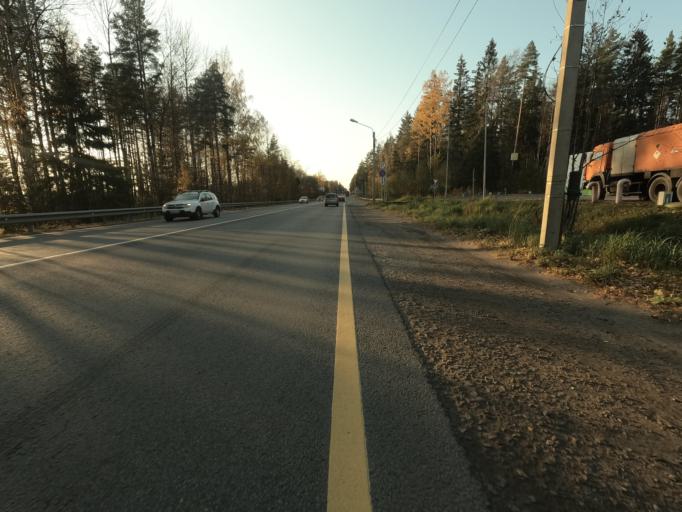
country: RU
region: St.-Petersburg
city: Pesochnyy
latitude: 60.1803
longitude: 30.1381
